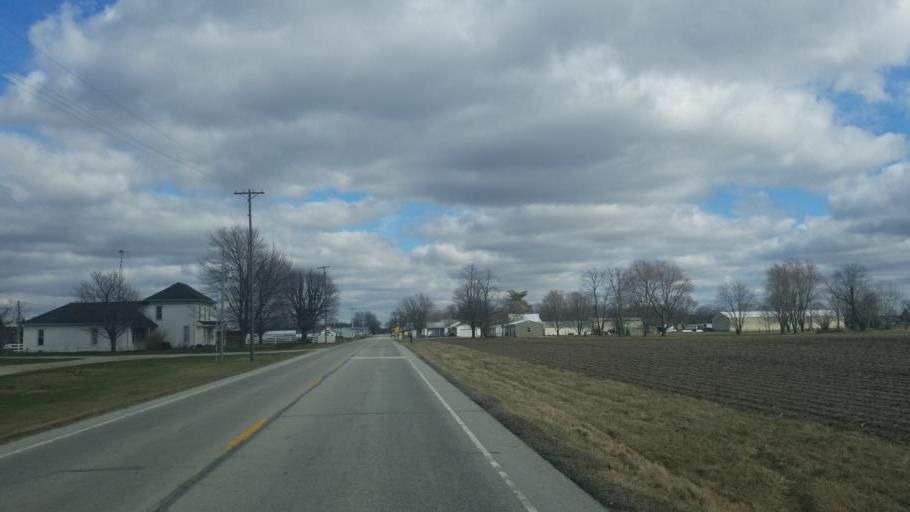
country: US
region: Indiana
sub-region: Parke County
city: Rockville
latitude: 39.7592
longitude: -87.1118
